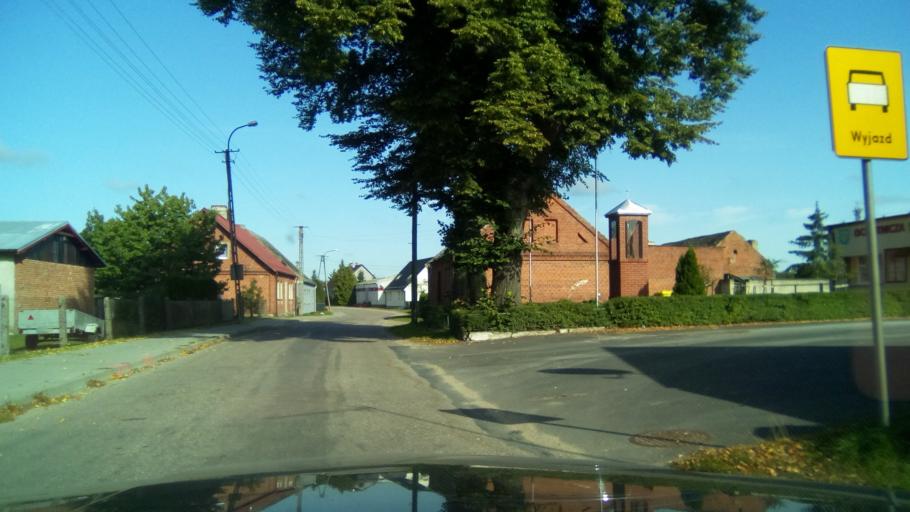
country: PL
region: Greater Poland Voivodeship
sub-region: Powiat zlotowski
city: Sypniewo
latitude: 53.3487
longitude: 16.5732
